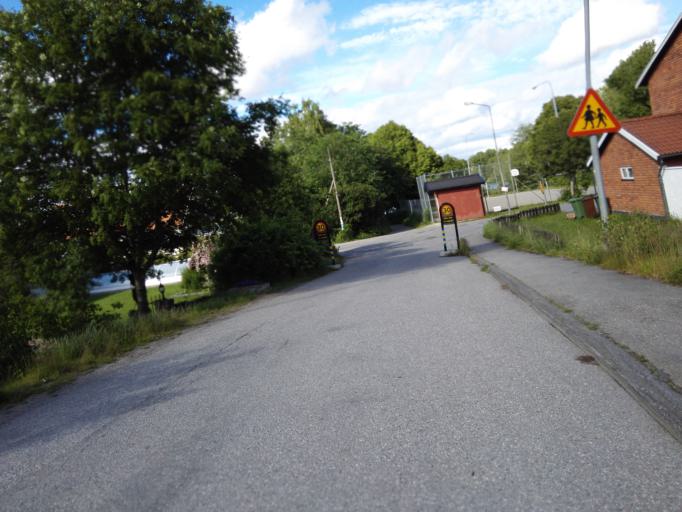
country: SE
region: Stockholm
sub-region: Huddinge Kommun
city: Huddinge
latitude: 59.2659
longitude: 17.9641
